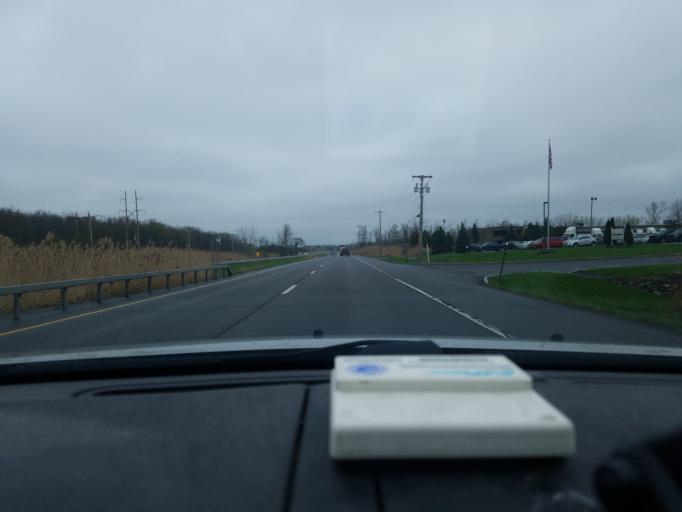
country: US
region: New York
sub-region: Onondaga County
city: East Syracuse
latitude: 43.1158
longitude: -76.0775
